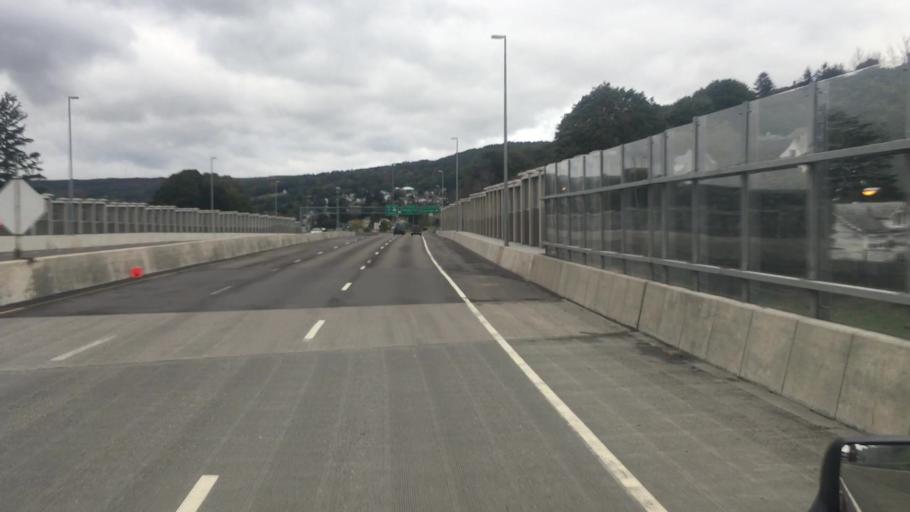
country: US
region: New York
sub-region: Broome County
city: Johnson City
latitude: 42.1175
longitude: -75.9406
